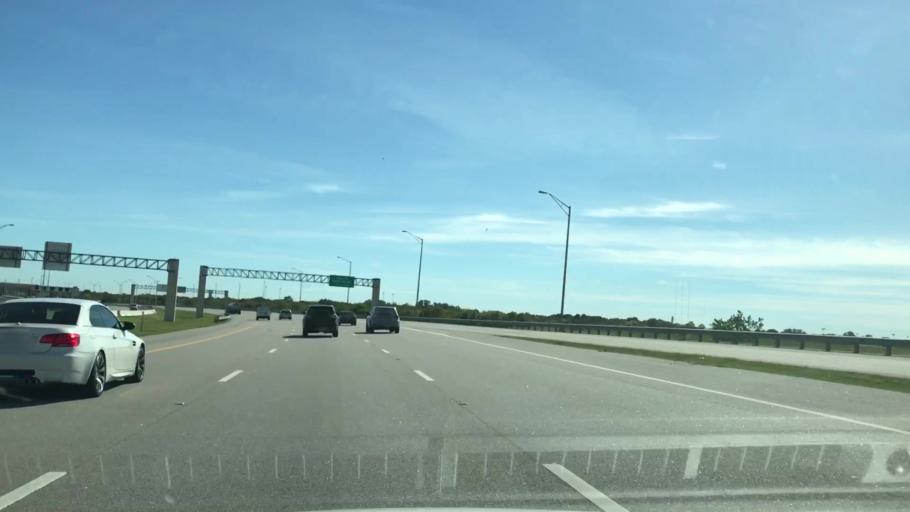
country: US
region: Texas
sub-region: Dallas County
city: Carrollton
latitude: 32.9652
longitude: -96.9331
